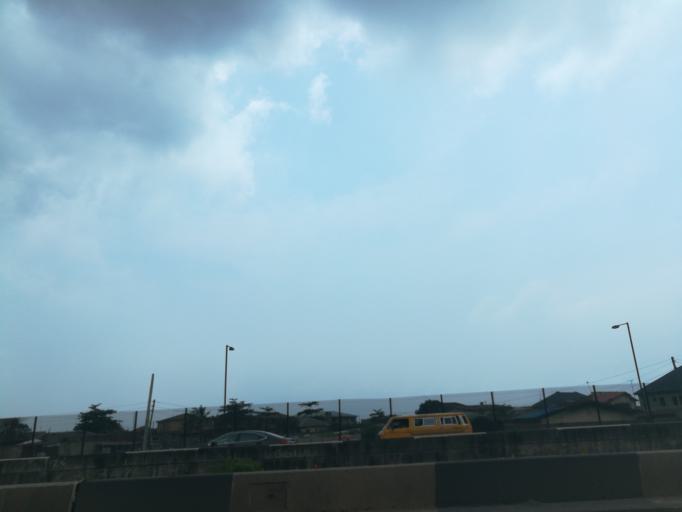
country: NG
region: Lagos
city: Ojota
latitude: 6.5600
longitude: 3.3954
